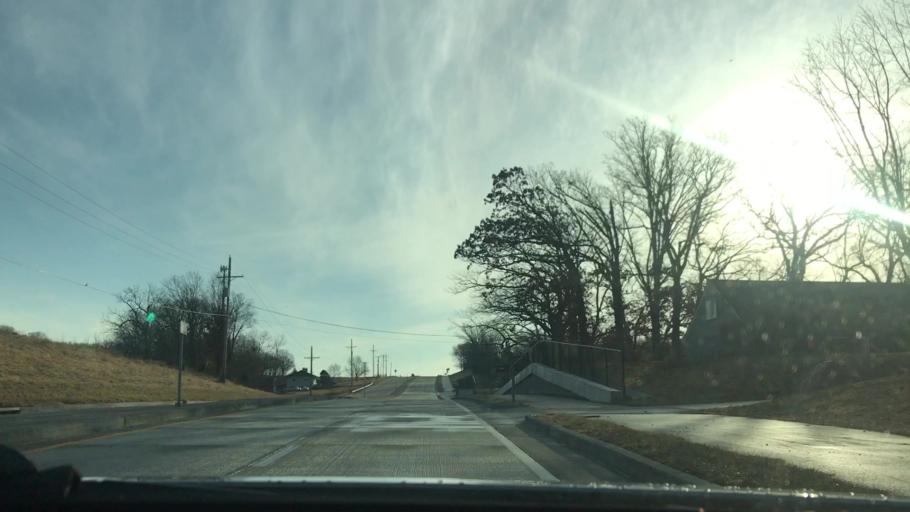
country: US
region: Missouri
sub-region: Platte County
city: Weatherby Lake
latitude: 39.2219
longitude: -94.7416
